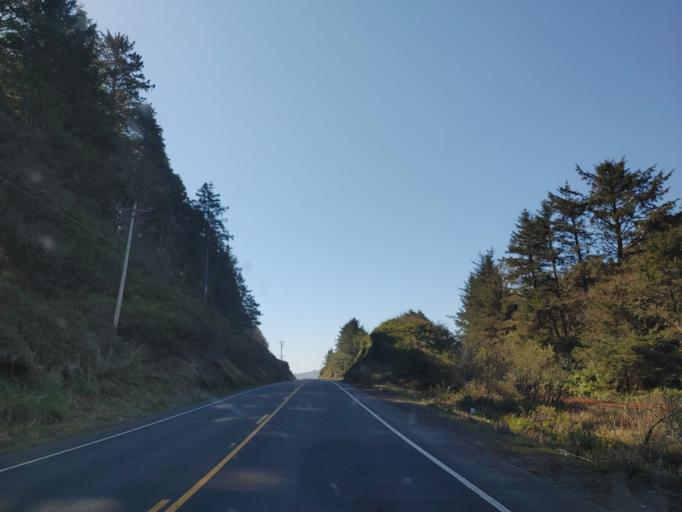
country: US
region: Oregon
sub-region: Tillamook County
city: Rockaway Beach
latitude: 45.5751
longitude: -123.9446
